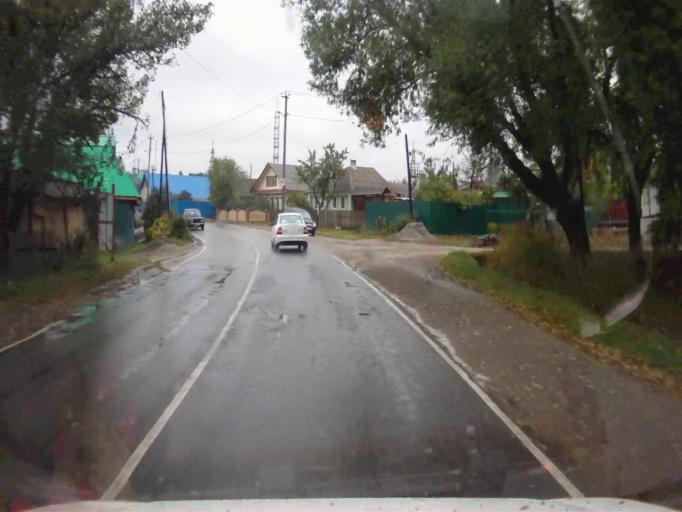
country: RU
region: Chelyabinsk
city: Kyshtym
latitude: 55.7246
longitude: 60.5241
